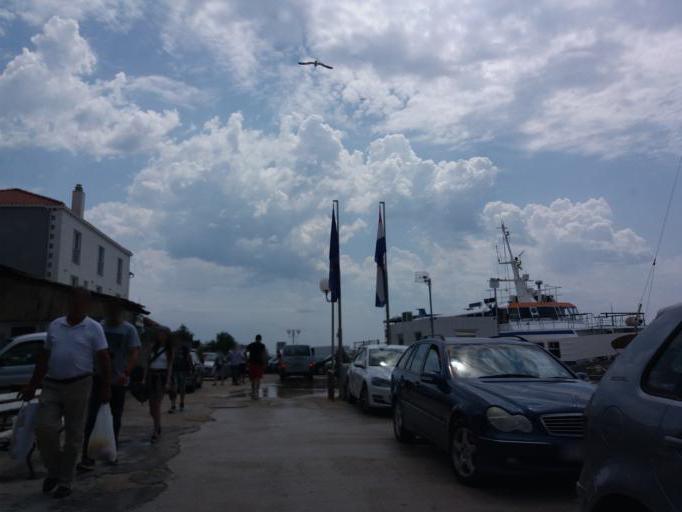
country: HR
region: Zadarska
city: Sali
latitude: 43.9372
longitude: 15.1671
